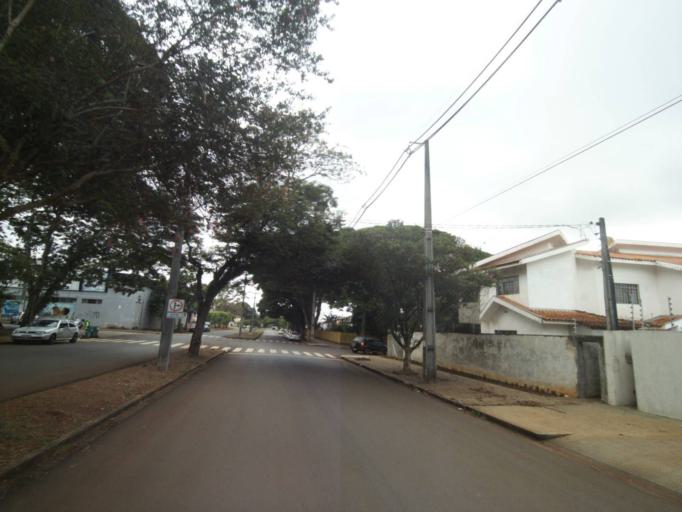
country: BR
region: Parana
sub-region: Campo Mourao
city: Campo Mourao
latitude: -24.0448
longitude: -52.3714
